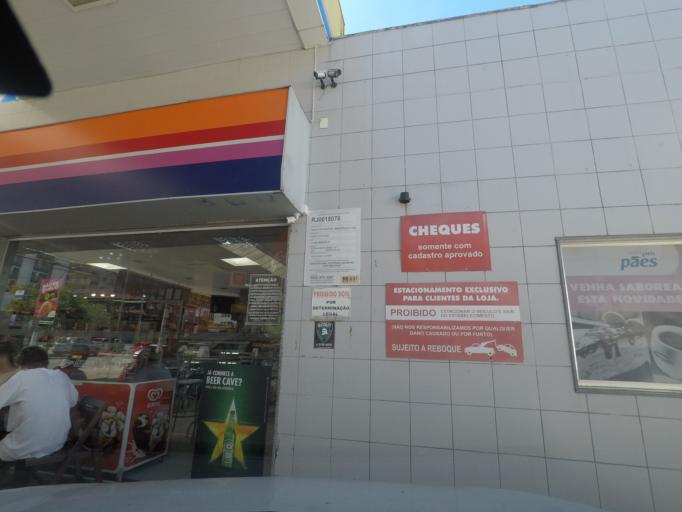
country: BR
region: Rio de Janeiro
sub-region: Teresopolis
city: Teresopolis
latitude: -22.4298
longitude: -42.9795
